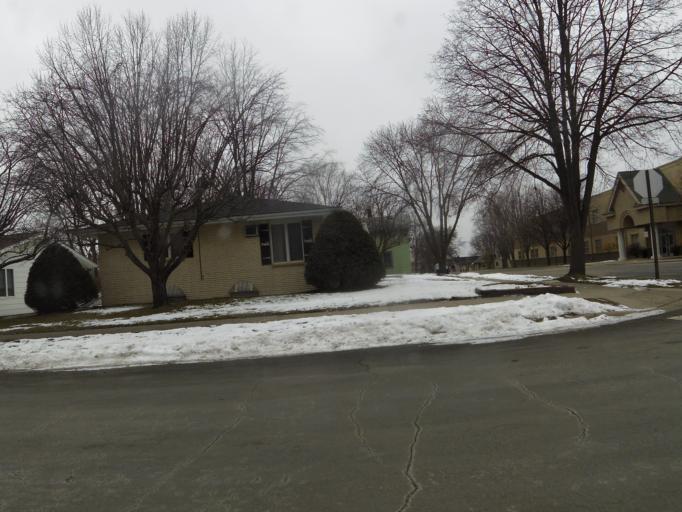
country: US
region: Minnesota
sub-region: Carver County
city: Waconia
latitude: 44.8482
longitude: -93.7846
